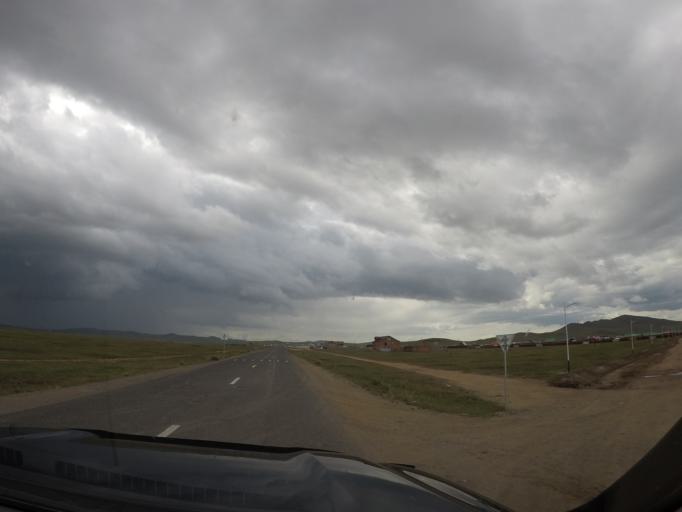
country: MN
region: Hentiy
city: Avraga
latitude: 47.4855
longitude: 109.4775
